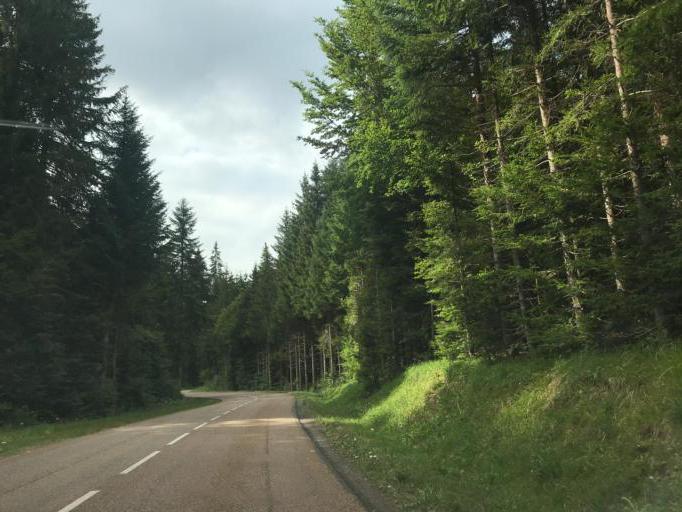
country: FR
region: Franche-Comte
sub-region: Departement du Jura
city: Longchaumois
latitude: 46.4999
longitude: 5.9180
